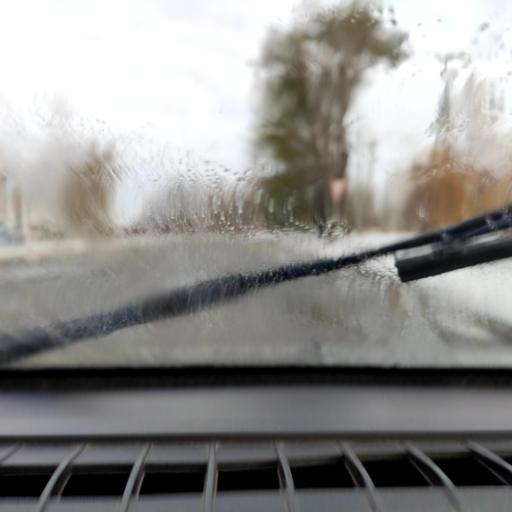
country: RU
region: Samara
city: Tol'yatti
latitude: 53.5786
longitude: 49.2845
